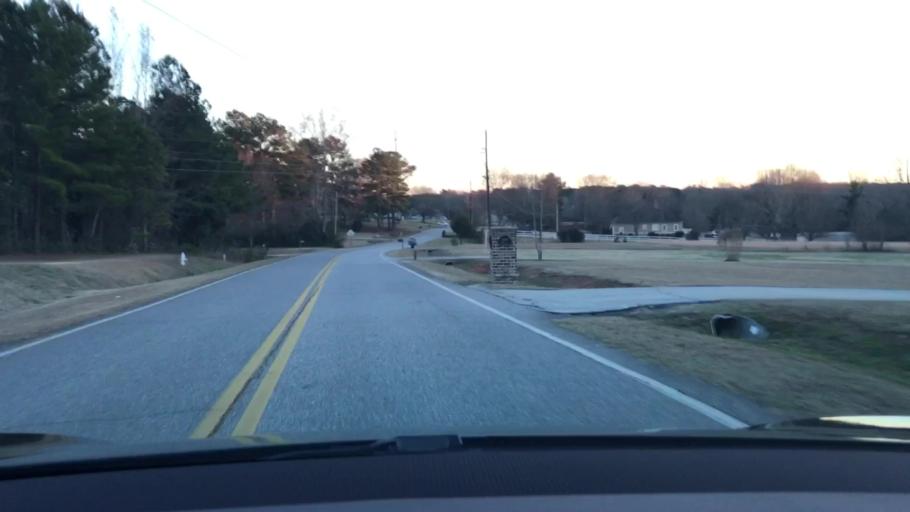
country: US
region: Georgia
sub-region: Gwinnett County
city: Grayson
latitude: 33.8860
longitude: -83.9154
